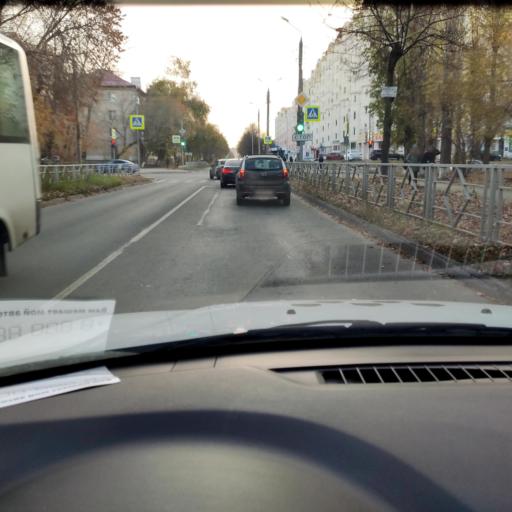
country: RU
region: Samara
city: Tol'yatti
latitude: 53.5048
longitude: 49.4072
